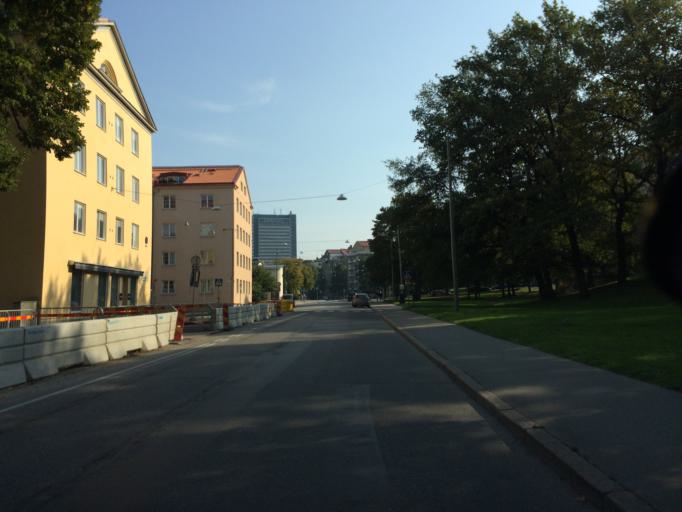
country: SE
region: Stockholm
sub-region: Solna Kommun
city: Solna
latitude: 59.3293
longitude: 18.0070
